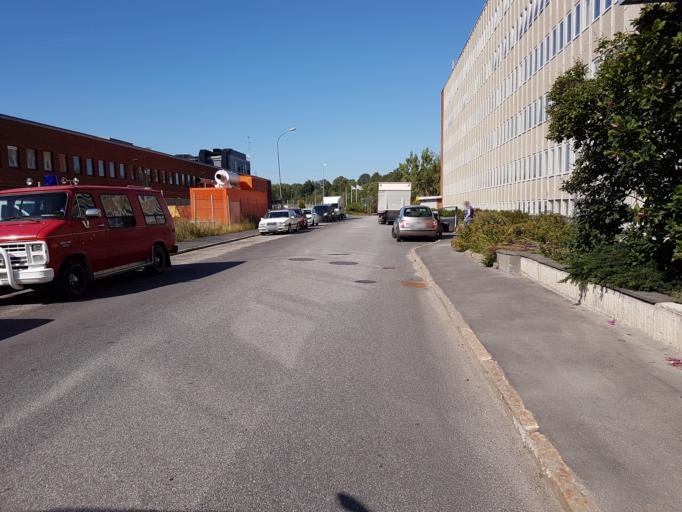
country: SE
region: Stockholm
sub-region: Huddinge Kommun
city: Huddinge
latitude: 59.2220
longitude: 17.9566
